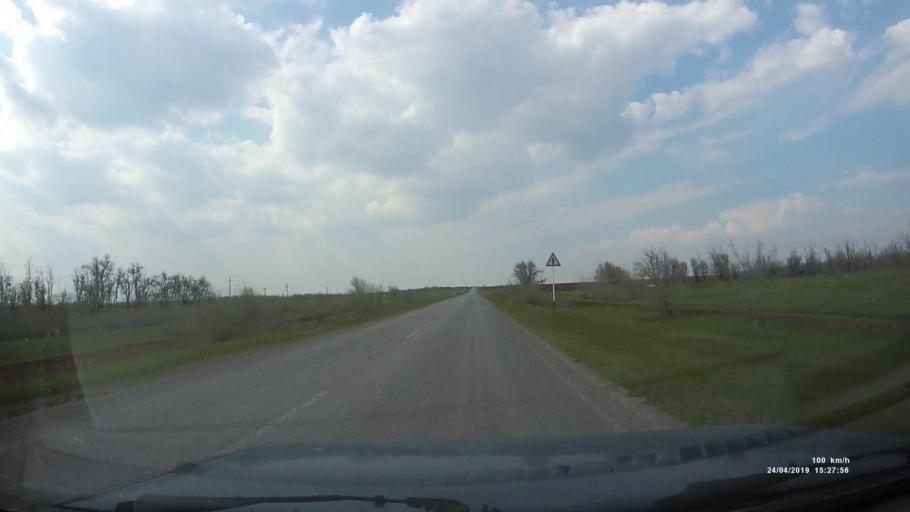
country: RU
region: Rostov
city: Remontnoye
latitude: 46.5718
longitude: 43.0221
